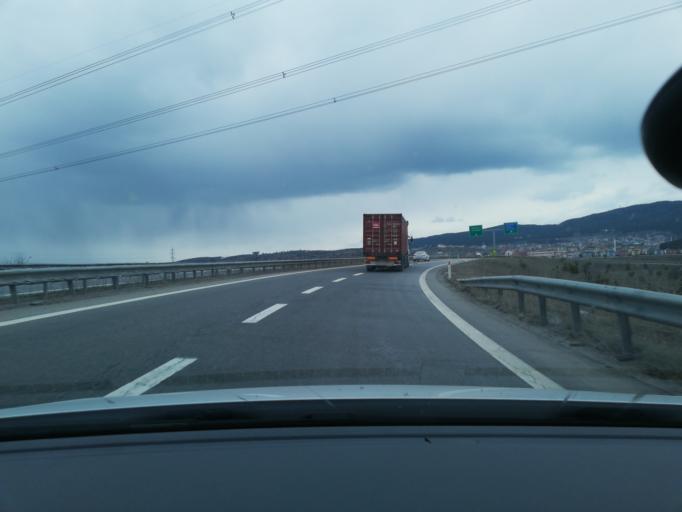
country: TR
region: Bolu
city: Gerede
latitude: 40.7771
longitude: 32.2122
